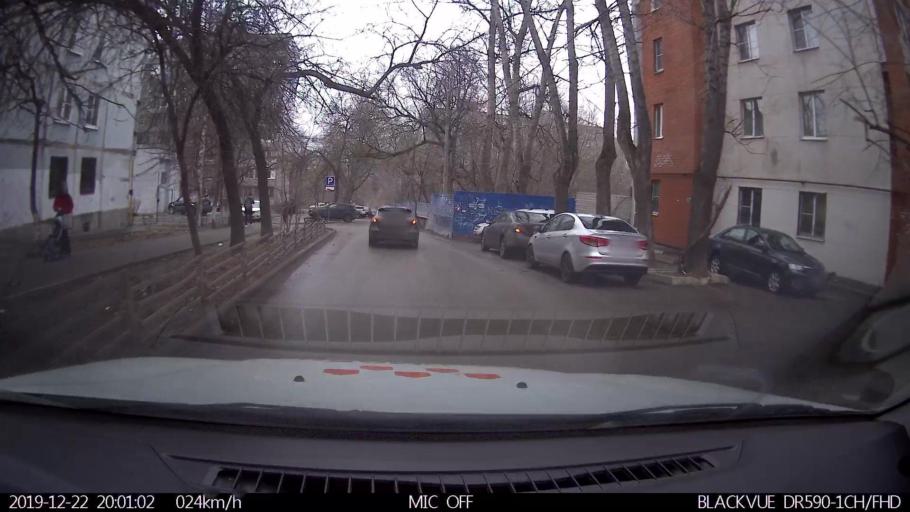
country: RU
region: Nizjnij Novgorod
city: Nizhniy Novgorod
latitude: 56.3201
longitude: 44.0245
